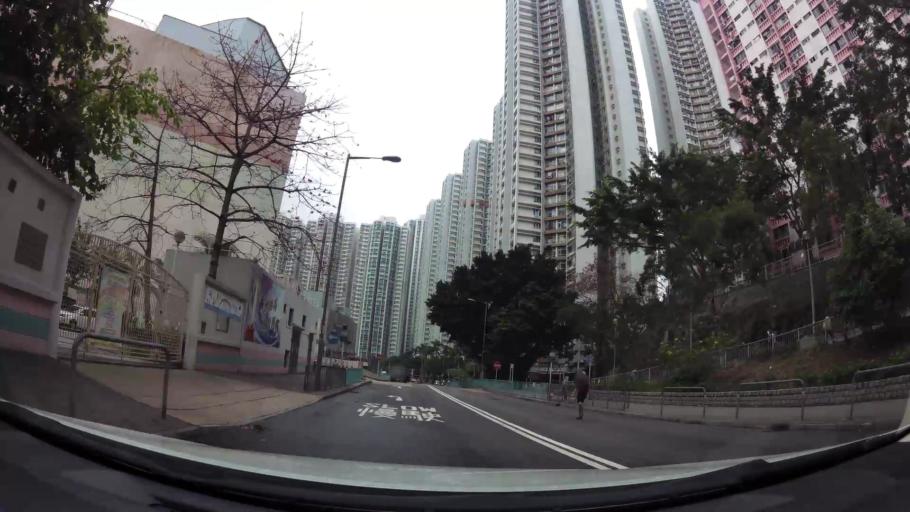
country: HK
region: Central and Western
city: Central
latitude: 22.2446
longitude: 114.1492
